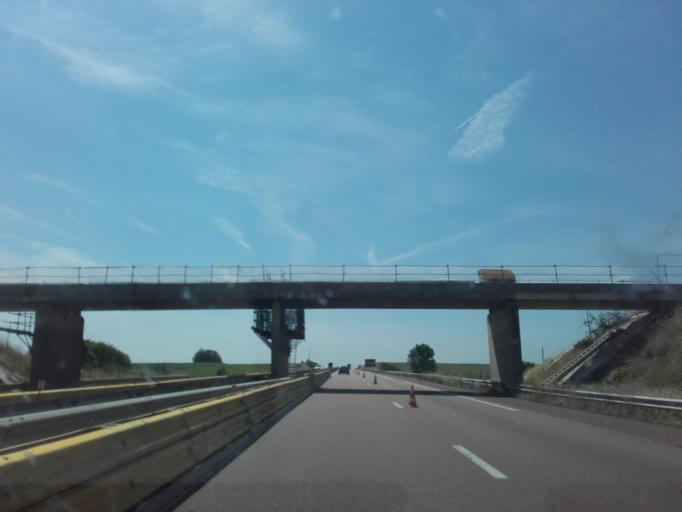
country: FR
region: Bourgogne
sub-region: Departement de l'Yonne
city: Joux-la-Ville
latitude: 47.5714
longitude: 3.9378
